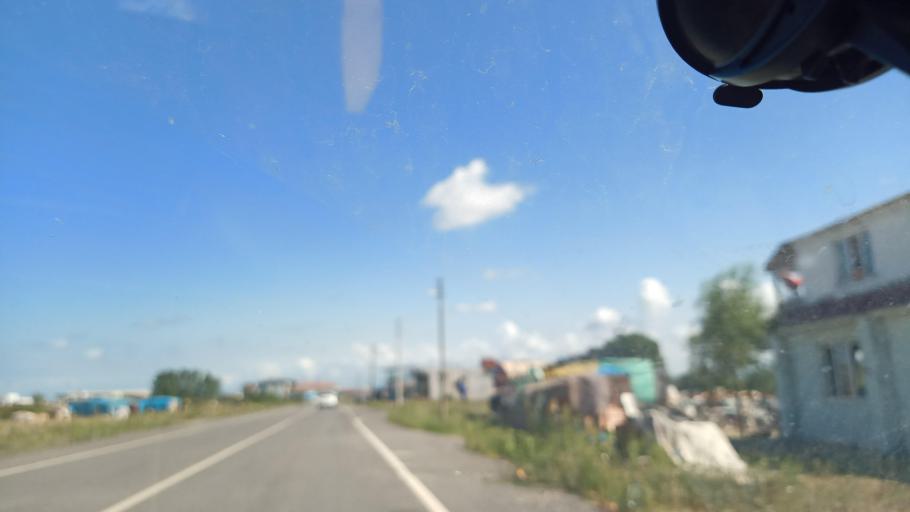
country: TR
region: Sakarya
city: Karasu
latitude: 41.1178
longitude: 30.6612
